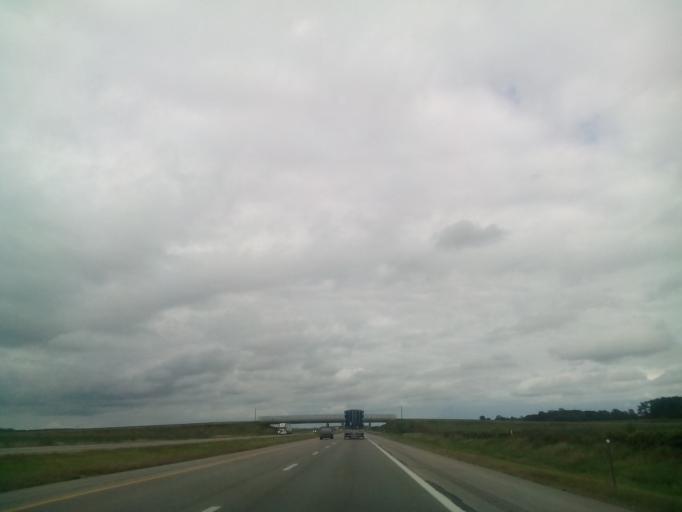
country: US
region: Ohio
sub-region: Fulton County
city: Burlington
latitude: 41.5905
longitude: -84.2723
